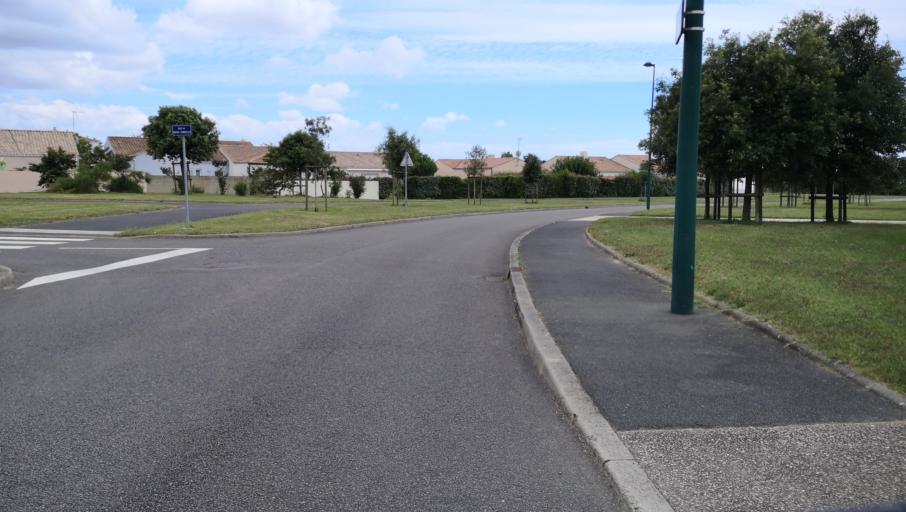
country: FR
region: Pays de la Loire
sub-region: Departement de la Vendee
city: Chateau-d'Olonne
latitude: 46.5066
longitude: -1.7591
